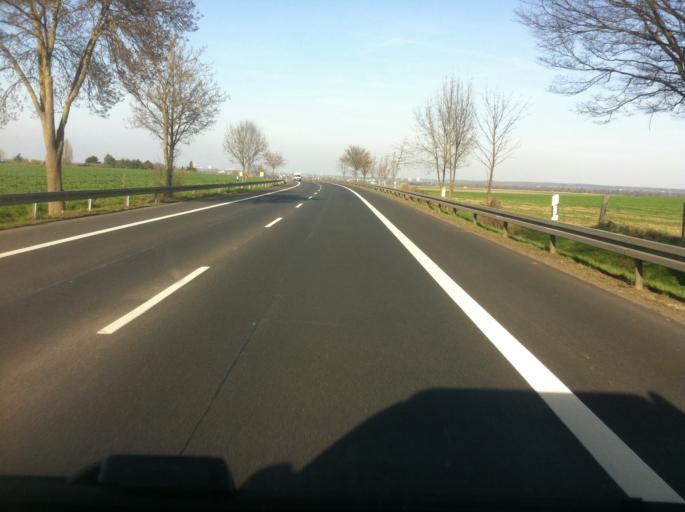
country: DE
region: North Rhine-Westphalia
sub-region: Regierungsbezirk Koln
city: Erftstadt
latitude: 50.7629
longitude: 6.7273
